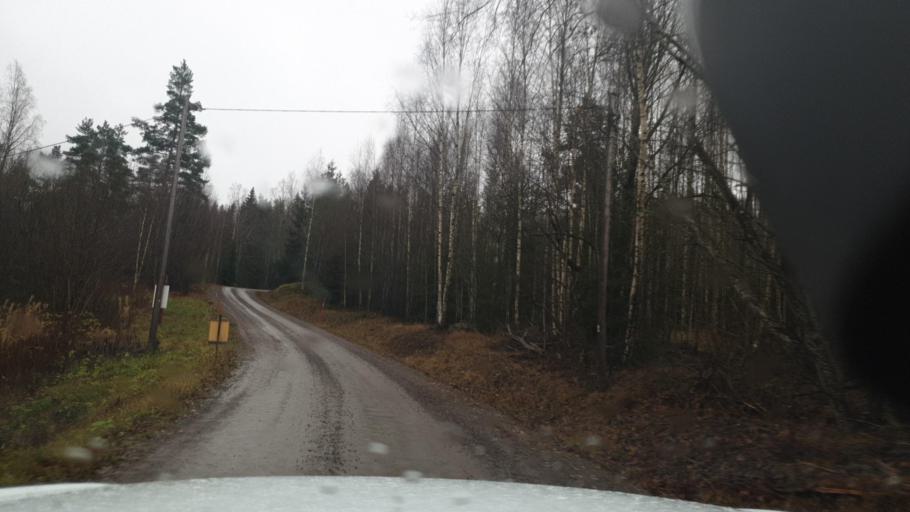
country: SE
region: Vaermland
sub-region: Grums Kommun
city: Grums
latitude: 59.4766
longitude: 12.9287
